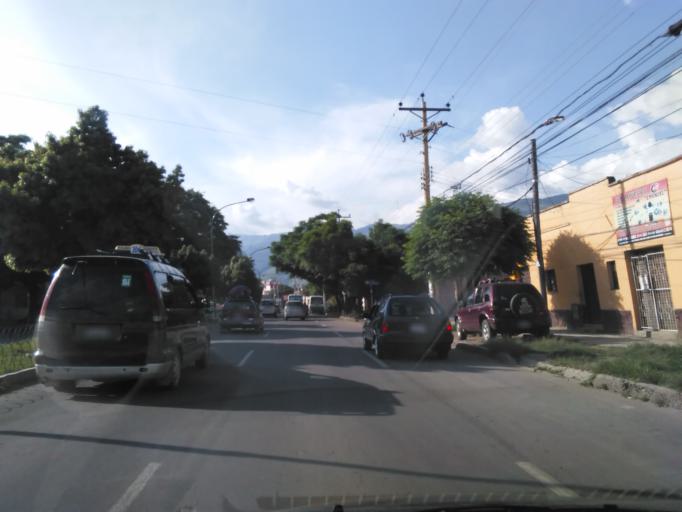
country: BO
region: Cochabamba
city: Cochabamba
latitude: -17.3602
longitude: -66.1825
